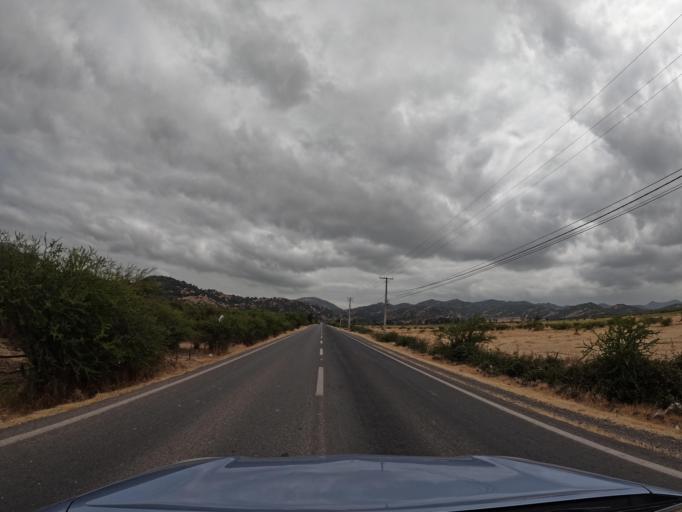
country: CL
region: Maule
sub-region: Provincia de Curico
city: Teno
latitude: -34.8377
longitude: -71.1880
